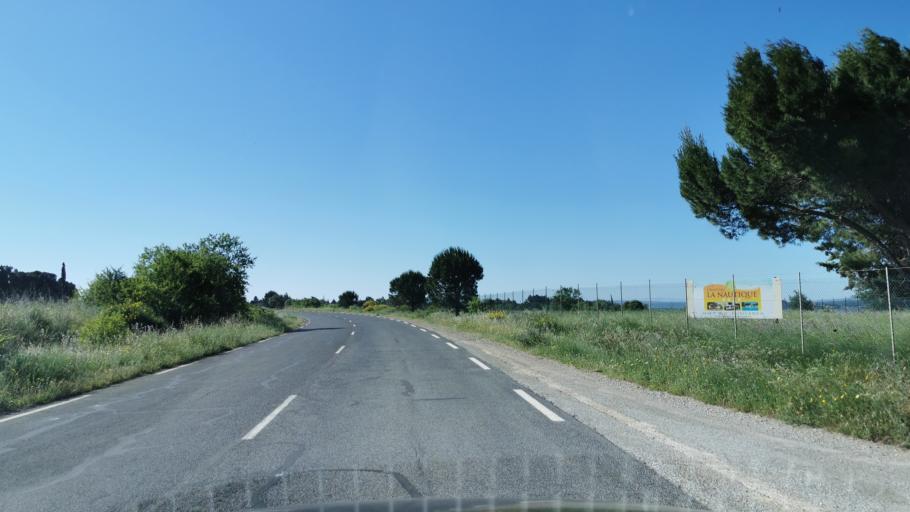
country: FR
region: Languedoc-Roussillon
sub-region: Departement de l'Aude
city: Narbonne
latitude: 43.1524
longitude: 2.9979
